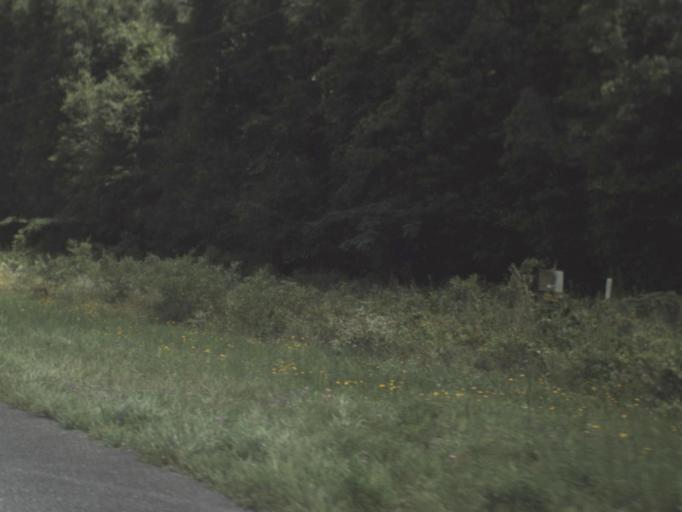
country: US
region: Florida
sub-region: Alachua County
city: High Springs
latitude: 29.8898
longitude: -82.6738
